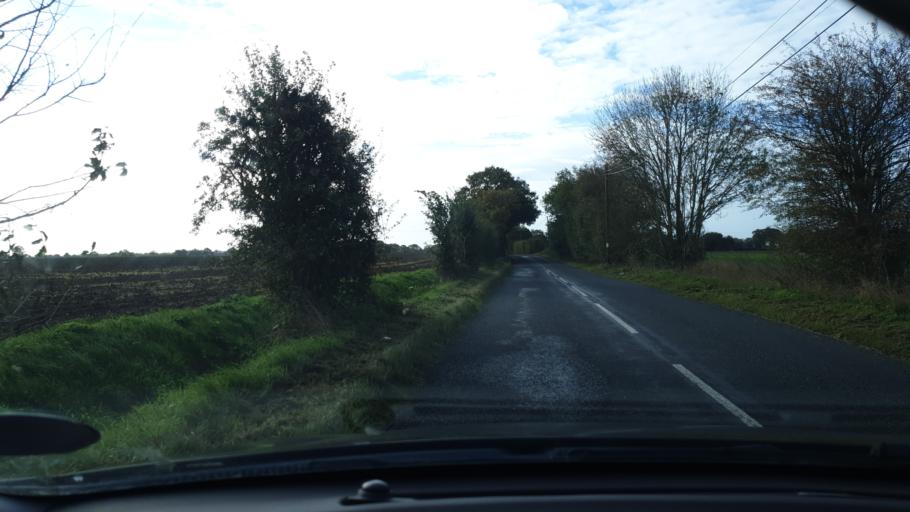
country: GB
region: England
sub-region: Essex
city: Manningtree
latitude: 51.9271
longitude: 1.0483
